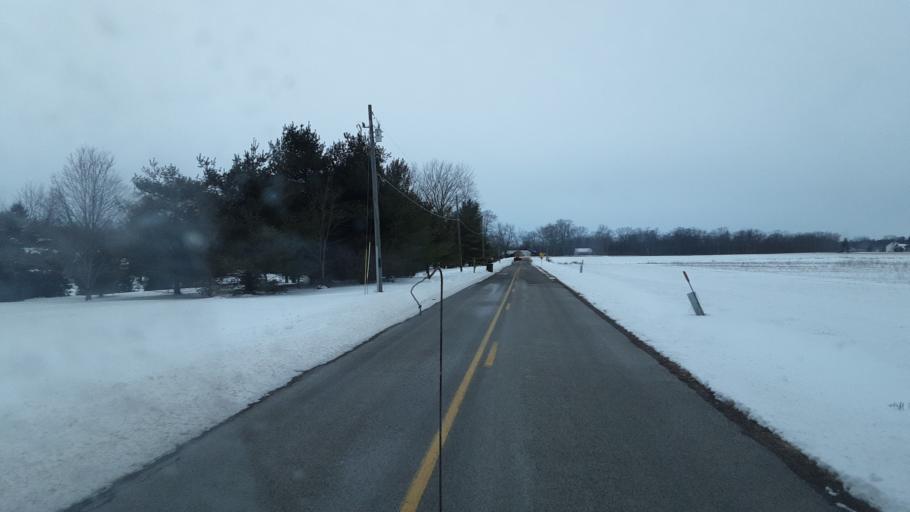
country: US
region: Ohio
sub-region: Madison County
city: Plain City
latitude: 40.1328
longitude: -83.3111
